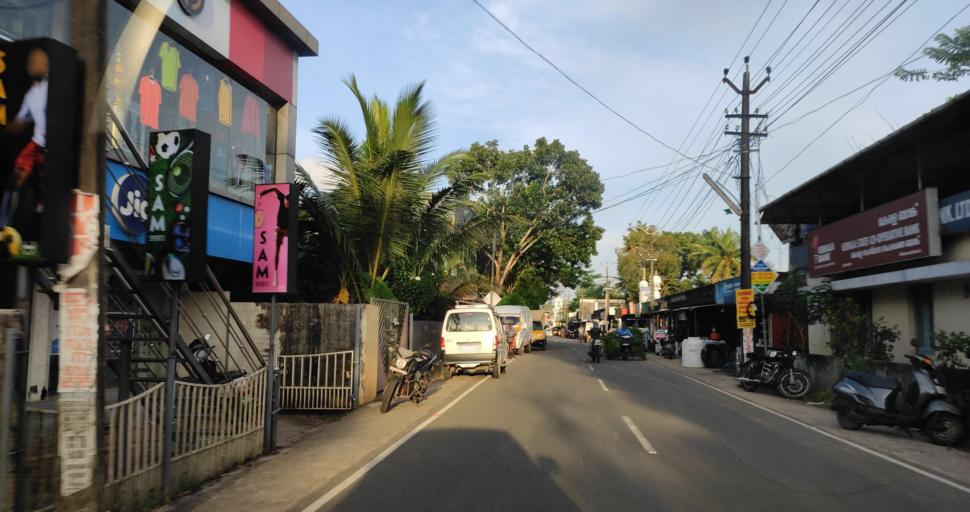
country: IN
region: Kerala
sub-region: Alappuzha
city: Shertallai
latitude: 9.6063
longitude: 76.3577
